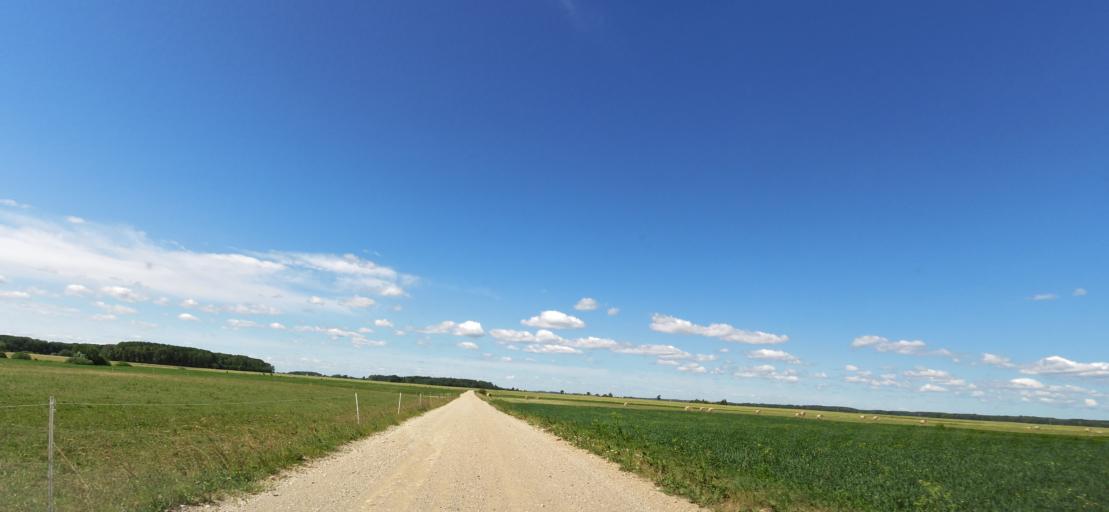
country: LT
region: Panevezys
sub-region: Birzai
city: Birzai
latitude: 56.2600
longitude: 24.5329
